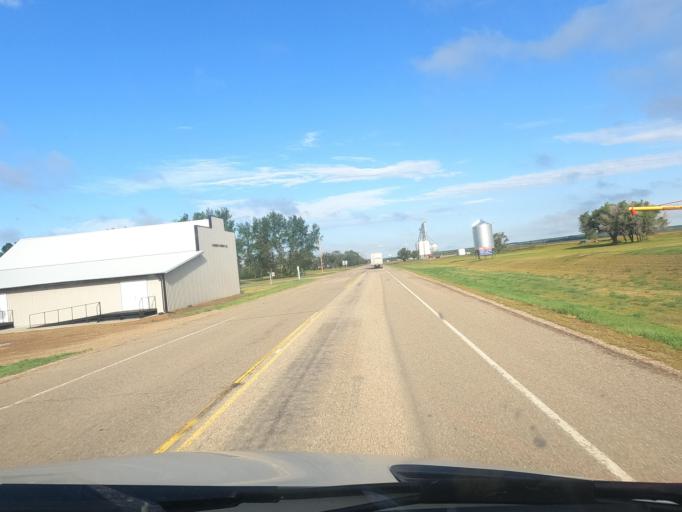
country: CA
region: Saskatchewan
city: Gravelbourg
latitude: 49.6883
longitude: -107.1361
